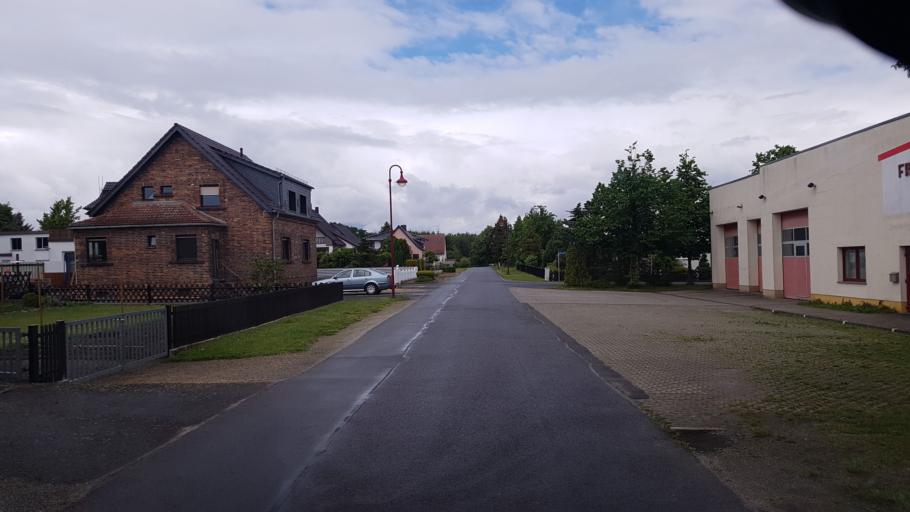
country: DE
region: Brandenburg
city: Hohenleipisch
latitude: 51.4981
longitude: 13.5661
